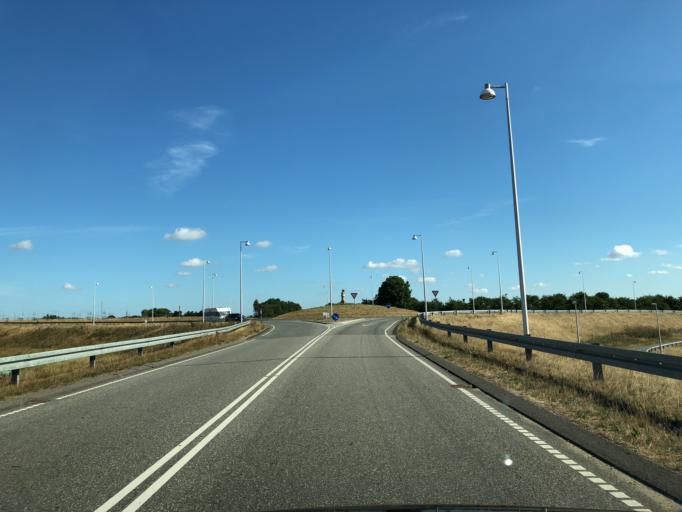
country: DK
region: Central Jutland
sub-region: Silkeborg Kommune
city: Silkeborg
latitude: 56.1501
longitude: 9.4561
